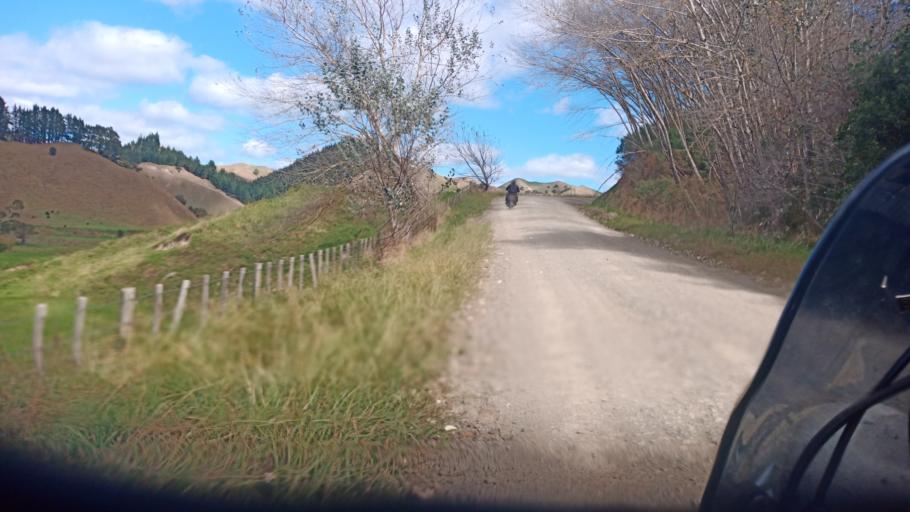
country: NZ
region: Gisborne
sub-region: Gisborne District
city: Gisborne
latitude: -38.4249
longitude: 177.7166
